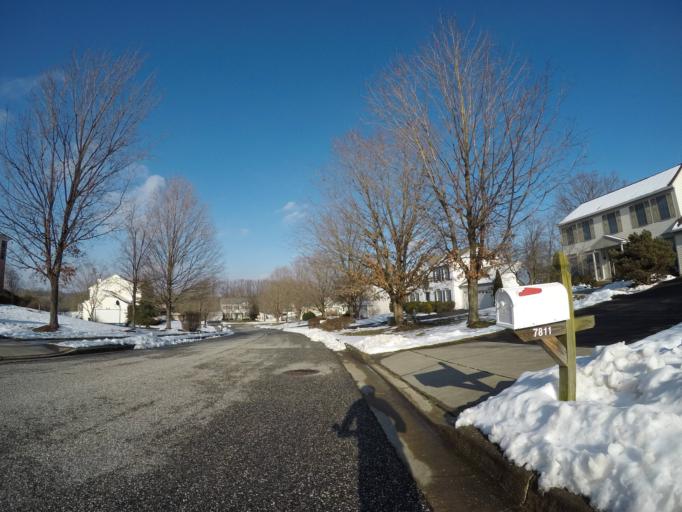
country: US
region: Maryland
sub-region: Howard County
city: Ilchester
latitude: 39.2158
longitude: -76.7812
